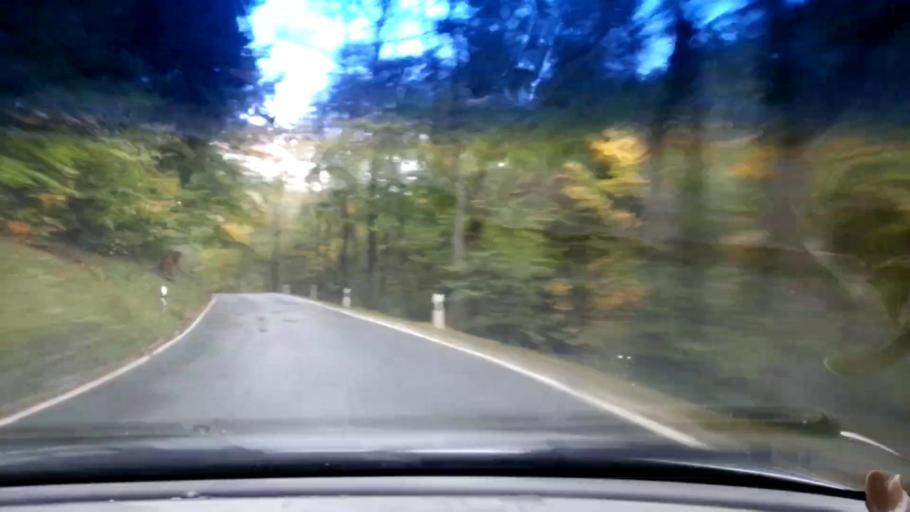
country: DE
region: Bavaria
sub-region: Upper Franconia
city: Stadelhofen
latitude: 50.0299
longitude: 11.2020
